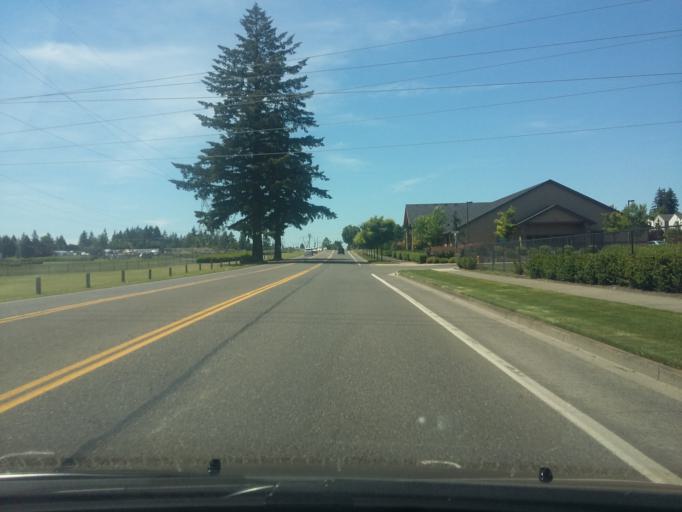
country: US
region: Washington
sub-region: Clark County
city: Mill Plain
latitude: 45.6357
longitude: -122.5001
